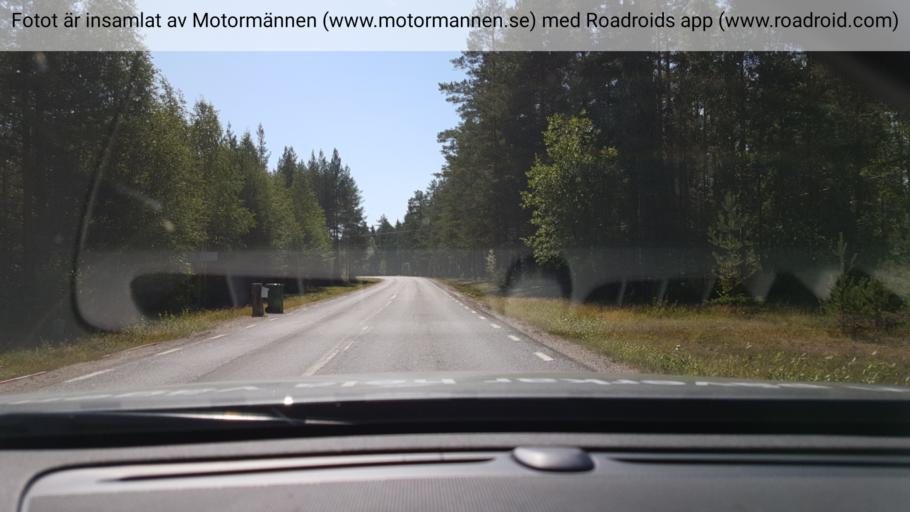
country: SE
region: Vaesterbotten
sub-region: Vindelns Kommun
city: Vindeln
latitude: 64.2854
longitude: 19.6198
